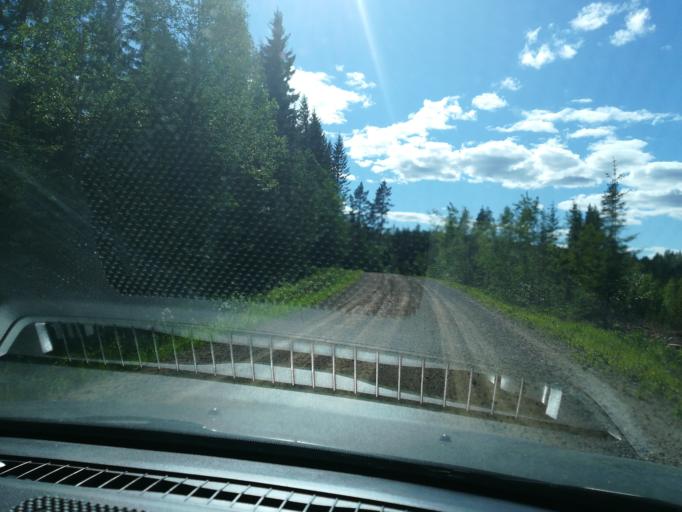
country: FI
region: Southern Savonia
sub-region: Mikkeli
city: Puumala
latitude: 61.6564
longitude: 28.1163
